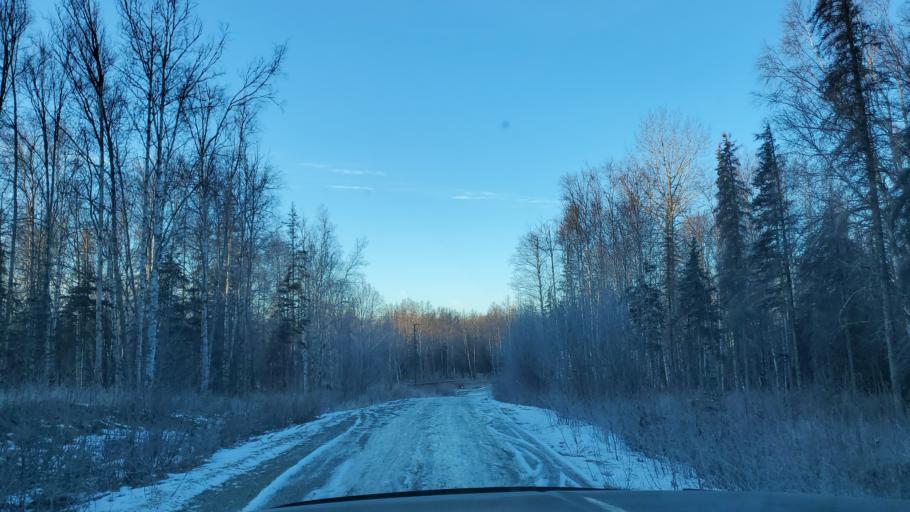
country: US
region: Alaska
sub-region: Matanuska-Susitna Borough
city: Lakes
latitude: 61.6537
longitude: -149.3342
